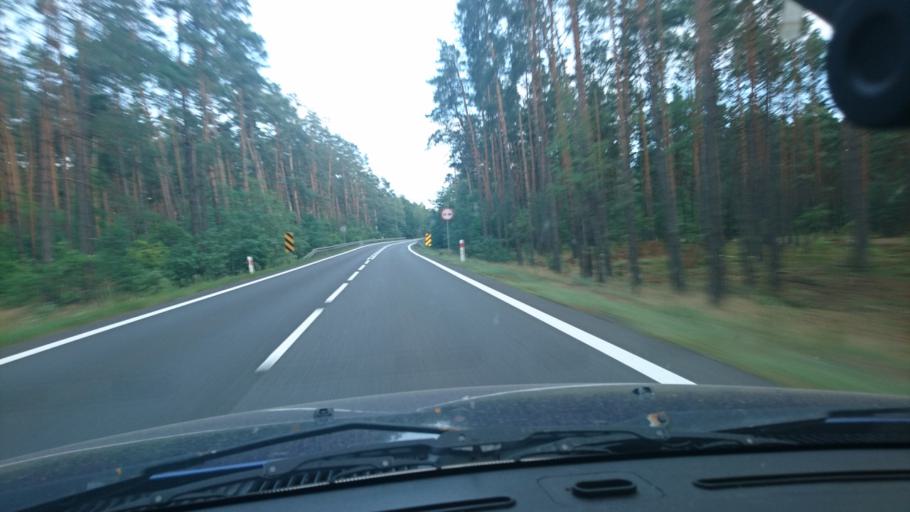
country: PL
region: Silesian Voivodeship
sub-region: Powiat lubliniecki
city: Lubliniec
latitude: 50.6030
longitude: 18.7002
